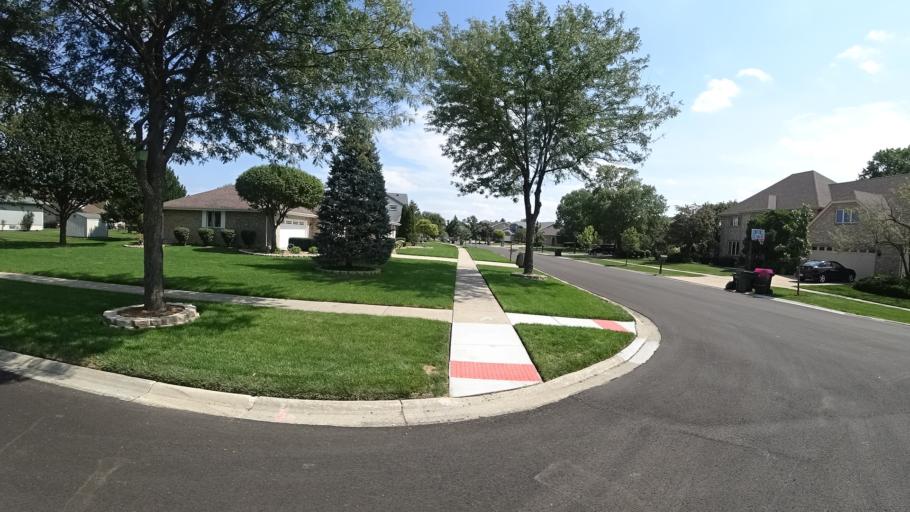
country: US
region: Illinois
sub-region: Cook County
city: Orland Hills
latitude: 41.5681
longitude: -87.8166
